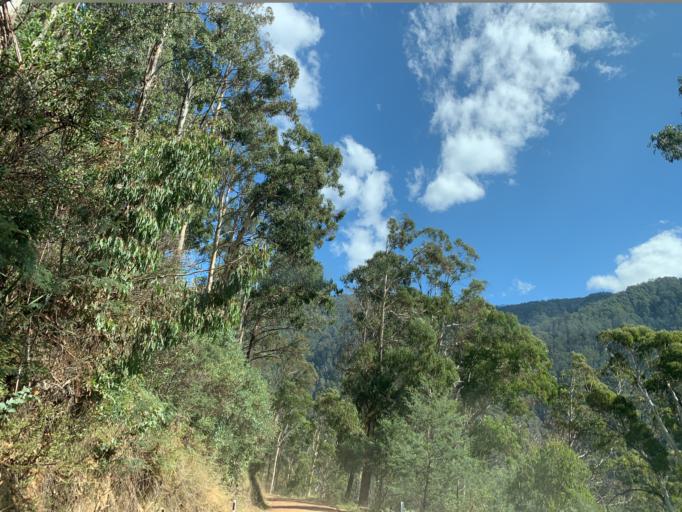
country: AU
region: Victoria
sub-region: Mansfield
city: Mansfield
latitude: -37.0998
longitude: 146.5047
